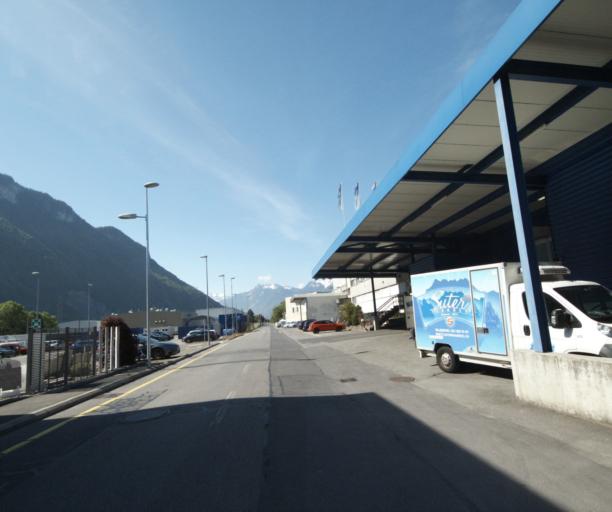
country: CH
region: Vaud
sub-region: Aigle District
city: Villeneuve
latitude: 46.3945
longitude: 6.9306
